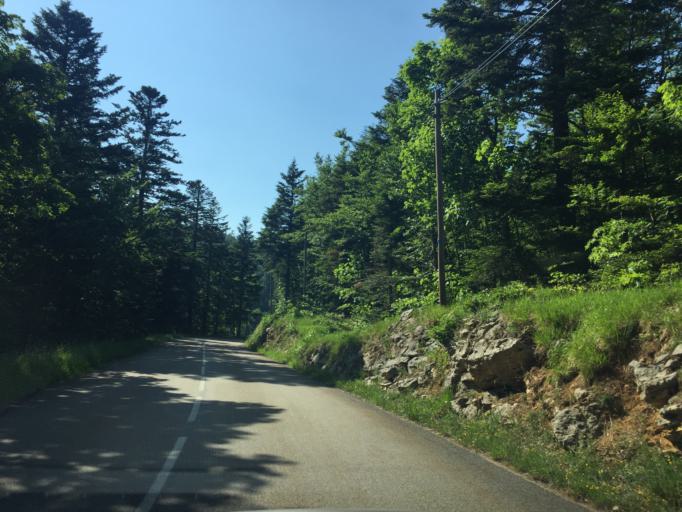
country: FR
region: Rhone-Alpes
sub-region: Departement de la Drome
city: Saint-Jean-en-Royans
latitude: 44.9201
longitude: 5.3248
